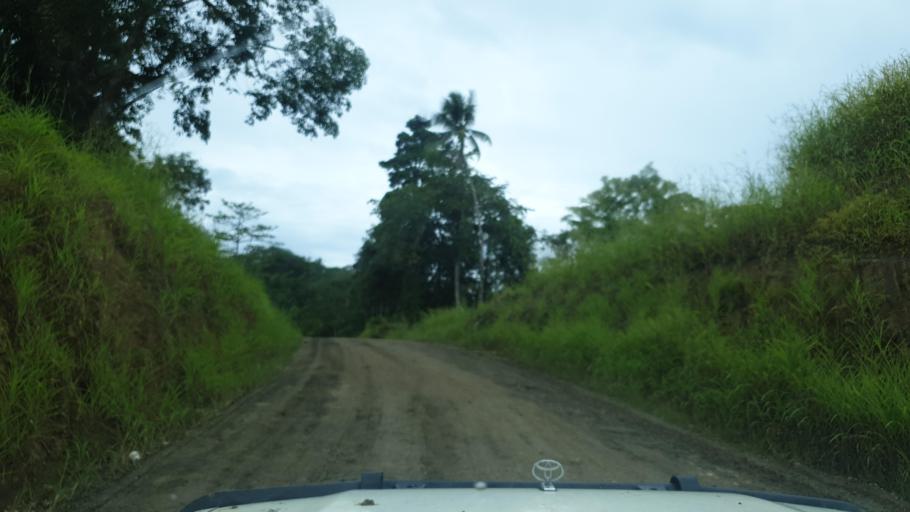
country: PG
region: Gulf
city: Kerema
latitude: -7.9803
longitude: 145.7896
